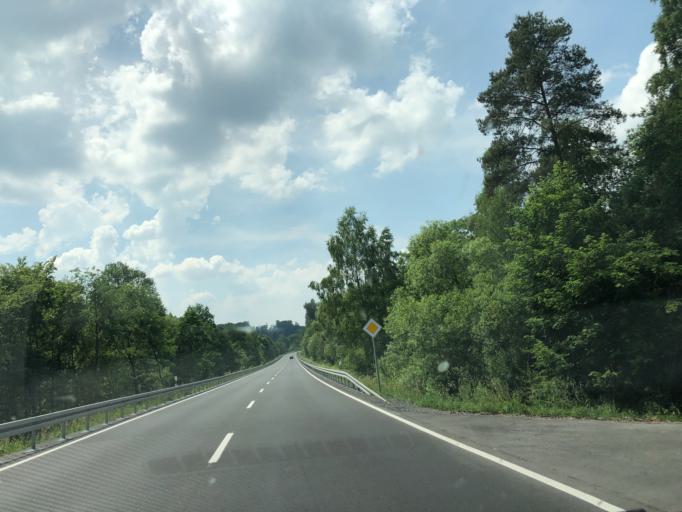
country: DE
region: Hesse
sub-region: Regierungsbezirk Kassel
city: Willingshausen
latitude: 50.8960
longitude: 9.1618
